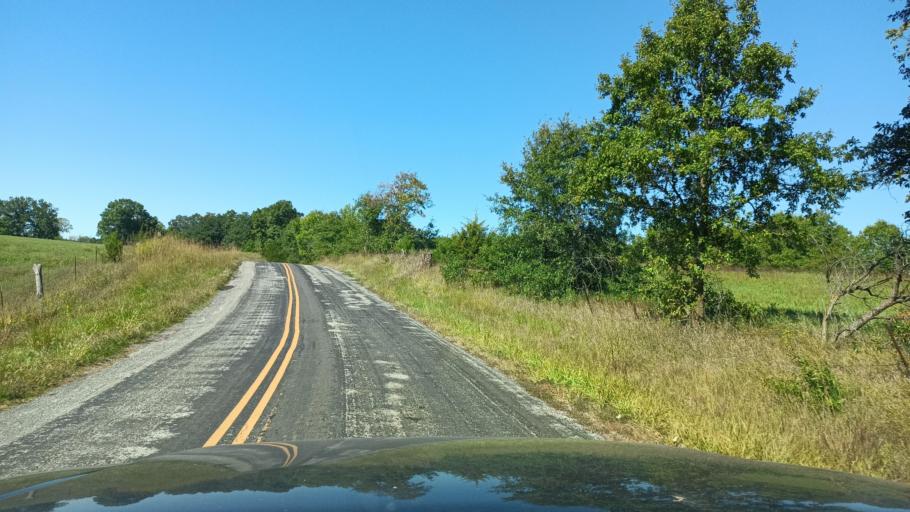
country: US
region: Missouri
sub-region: Scotland County
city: Memphis
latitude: 40.3538
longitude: -92.3474
